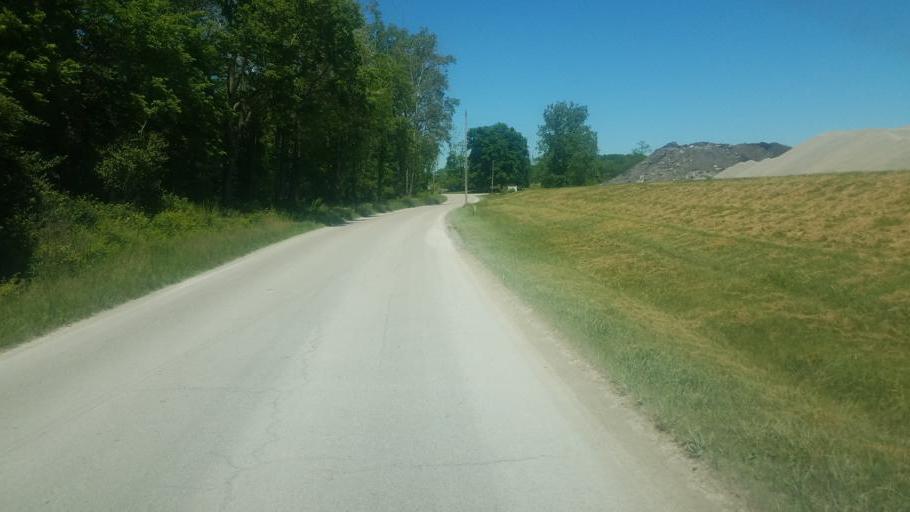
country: US
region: Ohio
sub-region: Miami County
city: Piqua
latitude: 40.2191
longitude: -84.2105
